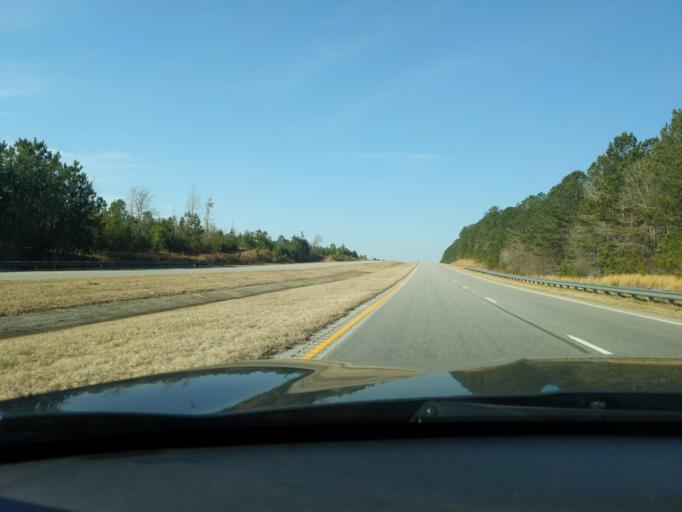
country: US
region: South Carolina
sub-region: Abbeville County
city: Calhoun Falls
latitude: 34.1130
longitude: -82.4837
